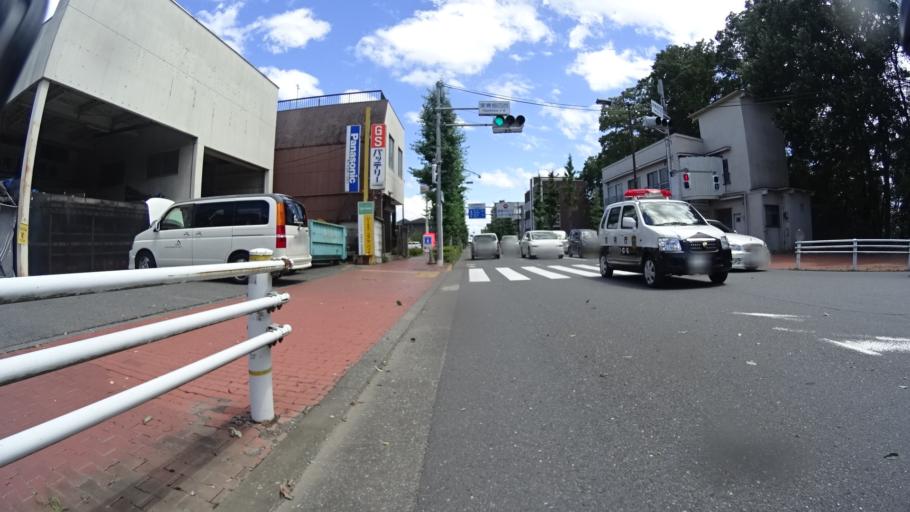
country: JP
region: Tokyo
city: Ome
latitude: 35.7867
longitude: 139.2774
